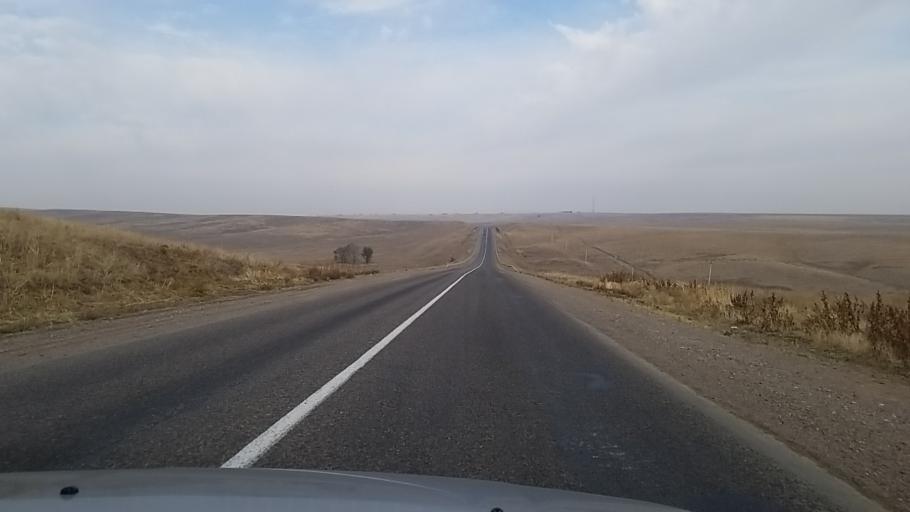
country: KZ
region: Almaty Oblysy
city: Burunday
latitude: 43.4892
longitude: 76.6684
